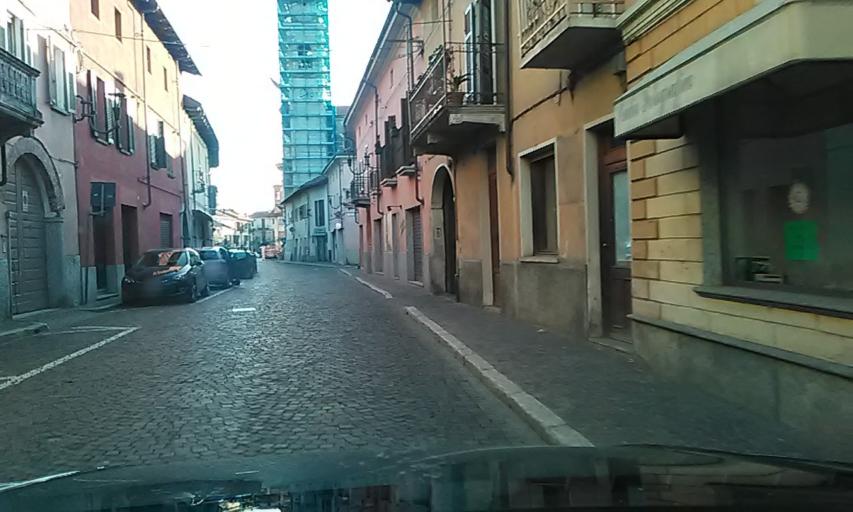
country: IT
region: Piedmont
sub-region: Provincia di Novara
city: Carpignano Sesia
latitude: 45.5358
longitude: 8.4192
